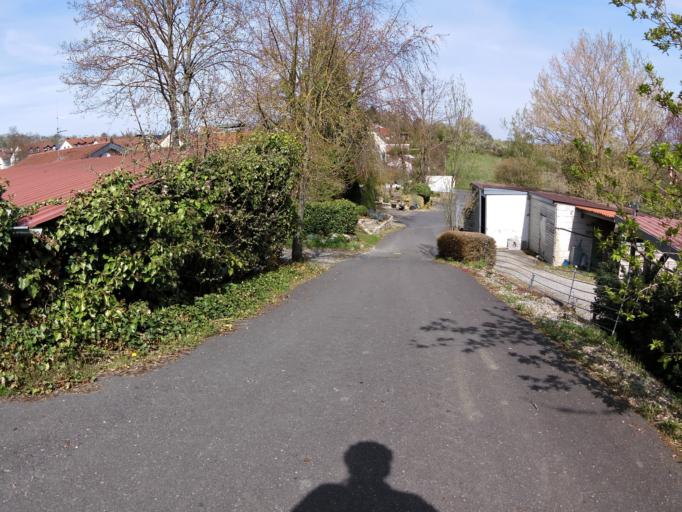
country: DE
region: Bavaria
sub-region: Regierungsbezirk Unterfranken
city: Dettelbach
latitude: 49.7974
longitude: 10.1527
